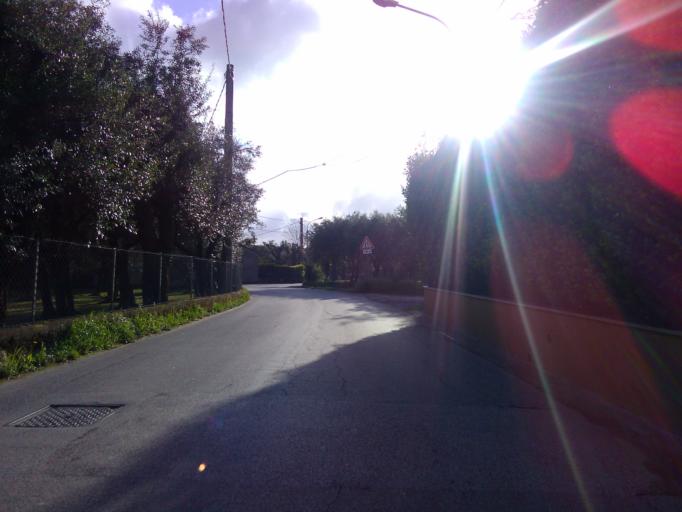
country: IT
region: Tuscany
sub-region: Provincia di Lucca
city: Strettoia
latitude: 43.9879
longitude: 10.1976
